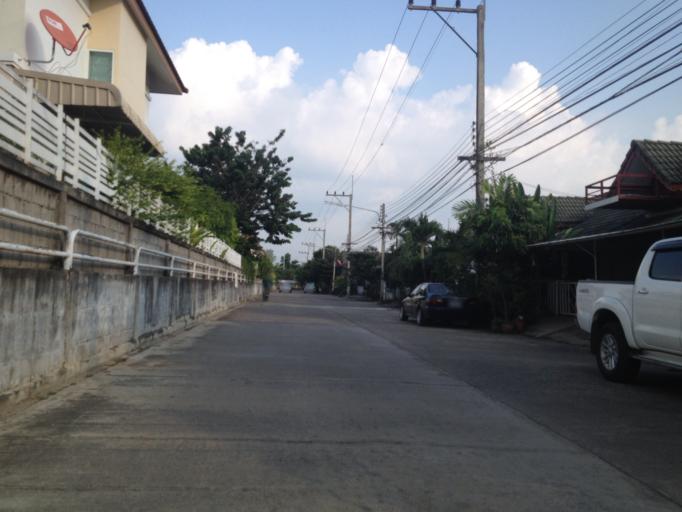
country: TH
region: Chiang Mai
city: Hang Dong
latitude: 18.7437
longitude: 98.9360
